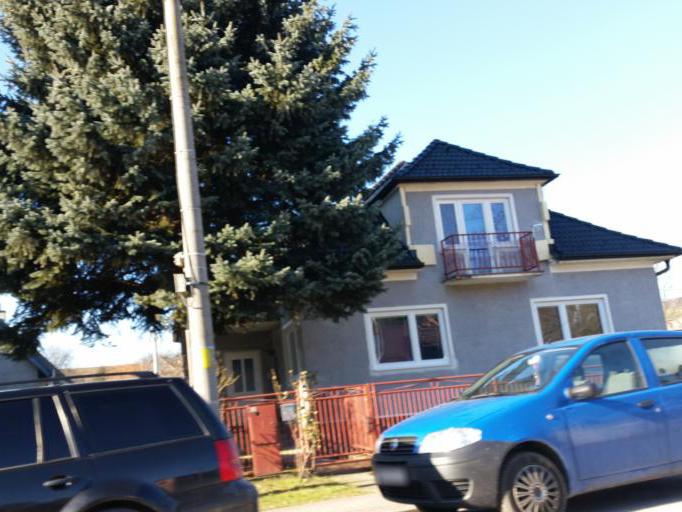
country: SK
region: Trnavsky
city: Vrbove
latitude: 48.6567
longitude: 17.7183
